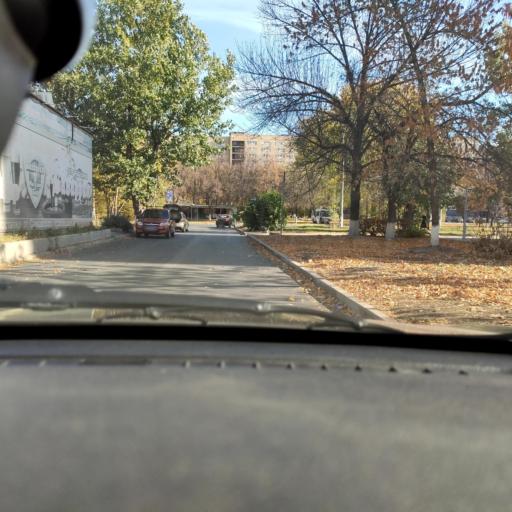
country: RU
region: Samara
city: Tol'yatti
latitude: 53.5330
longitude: 49.2761
